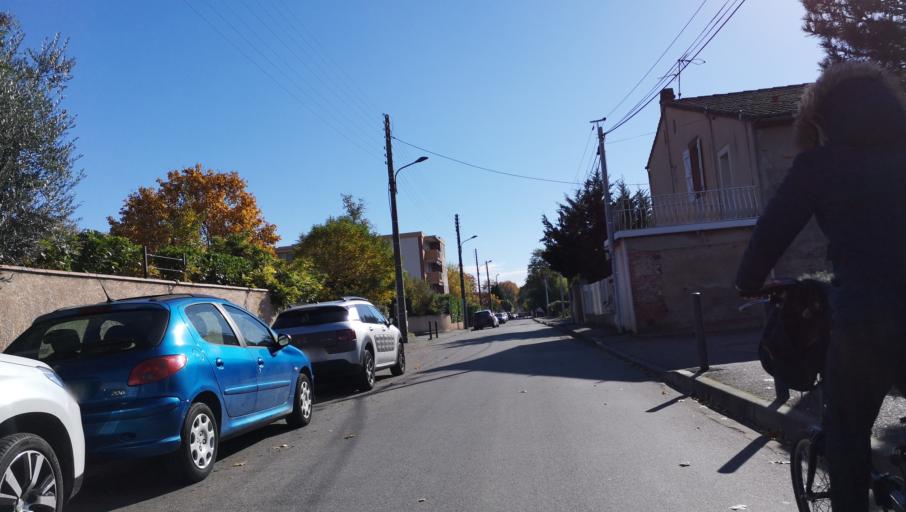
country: FR
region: Midi-Pyrenees
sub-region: Departement de la Haute-Garonne
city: Blagnac
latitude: 43.6204
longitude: 1.4046
